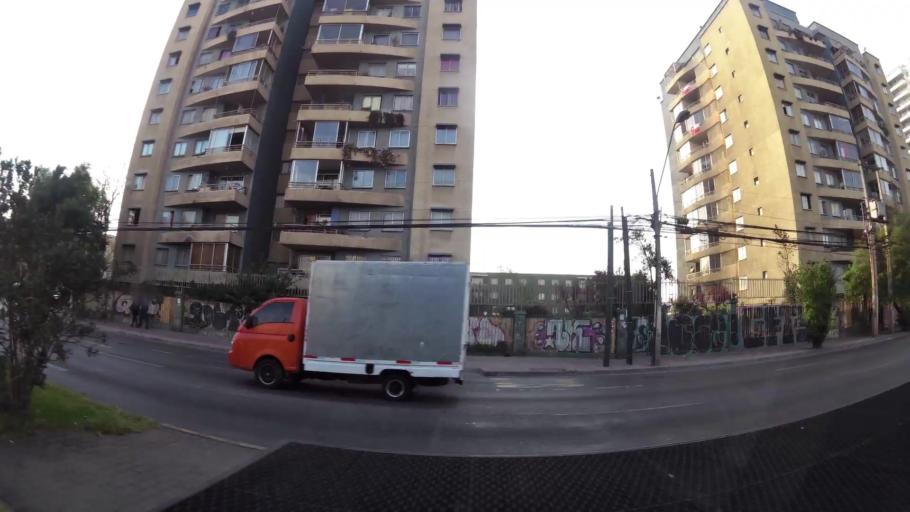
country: CL
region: Santiago Metropolitan
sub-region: Provincia de Santiago
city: Santiago
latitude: -33.5133
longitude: -70.6578
